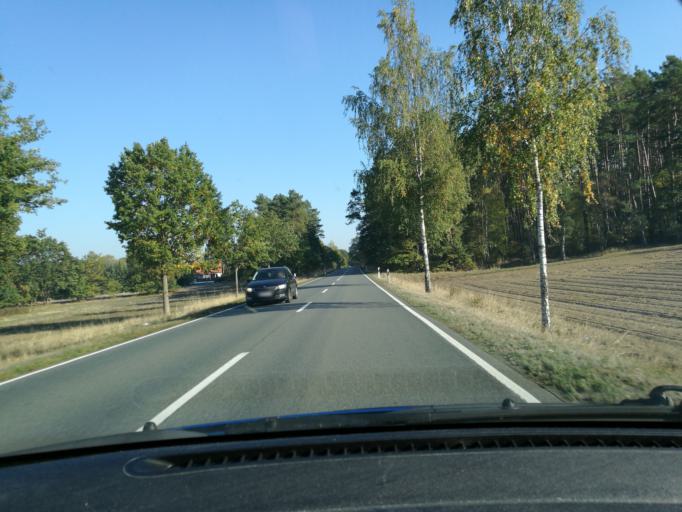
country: DE
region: Lower Saxony
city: Karwitz
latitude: 53.1061
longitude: 11.0331
